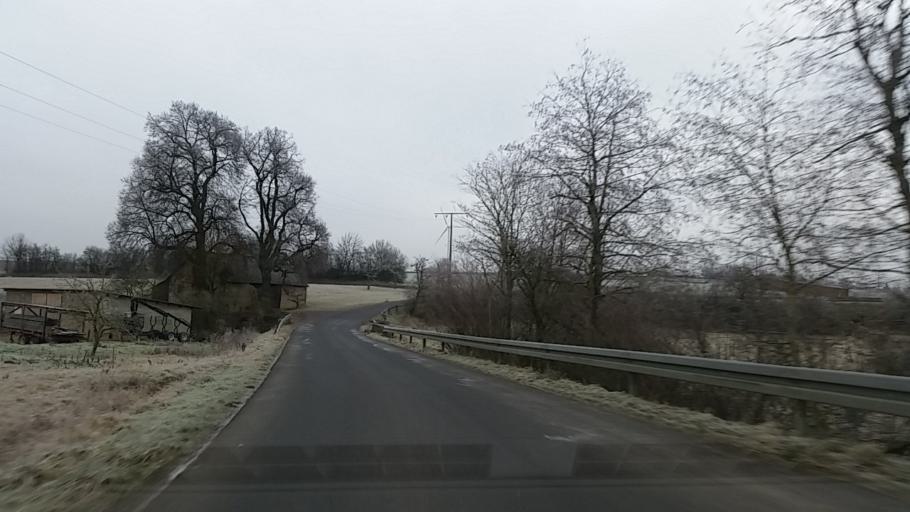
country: DE
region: Bavaria
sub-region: Regierungsbezirk Unterfranken
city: Fuchsstadt
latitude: 50.0490
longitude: 9.9206
